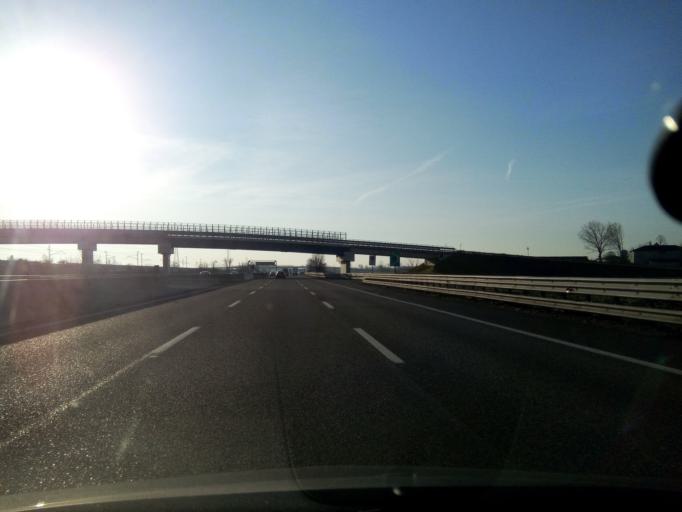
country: IT
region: Emilia-Romagna
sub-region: Provincia di Piacenza
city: Fiorenzuola d'Arda
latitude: 44.9493
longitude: 9.9365
